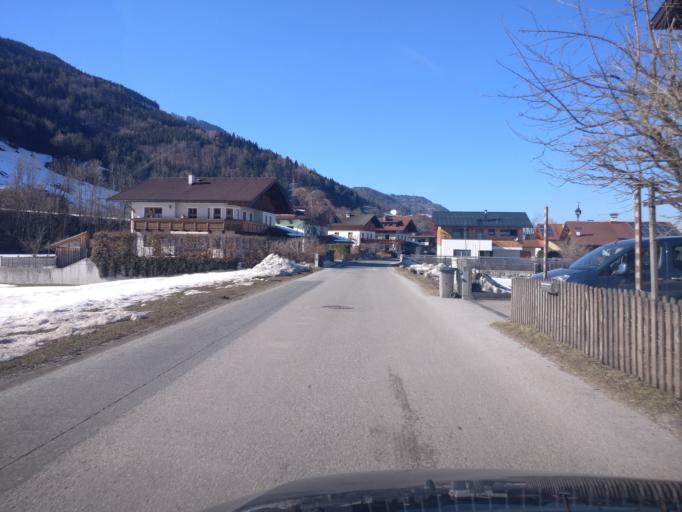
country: AT
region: Salzburg
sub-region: Politischer Bezirk Hallein
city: Kuchl
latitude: 47.6147
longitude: 13.1430
